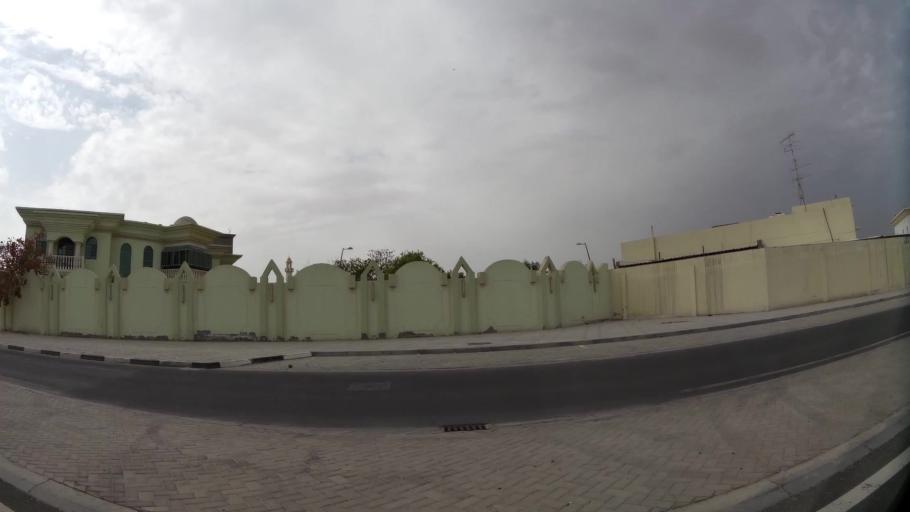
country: QA
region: Baladiyat ad Dawhah
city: Doha
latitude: 25.3458
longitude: 51.4935
